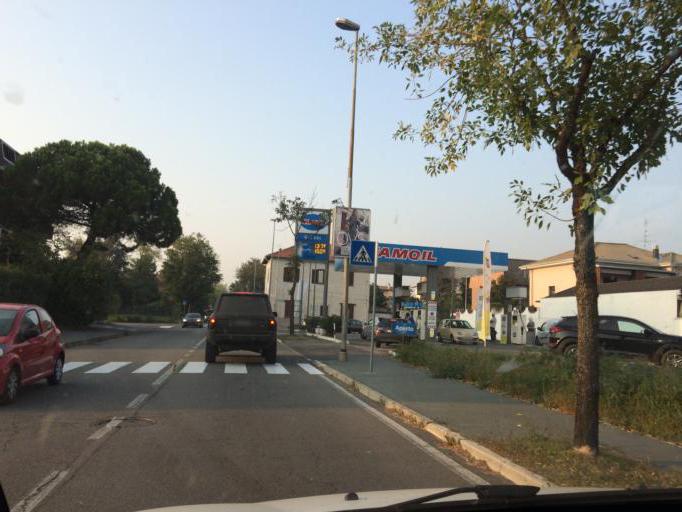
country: IT
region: Lombardy
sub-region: Citta metropolitana di Milano
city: Legnano
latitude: 45.5925
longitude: 8.8992
